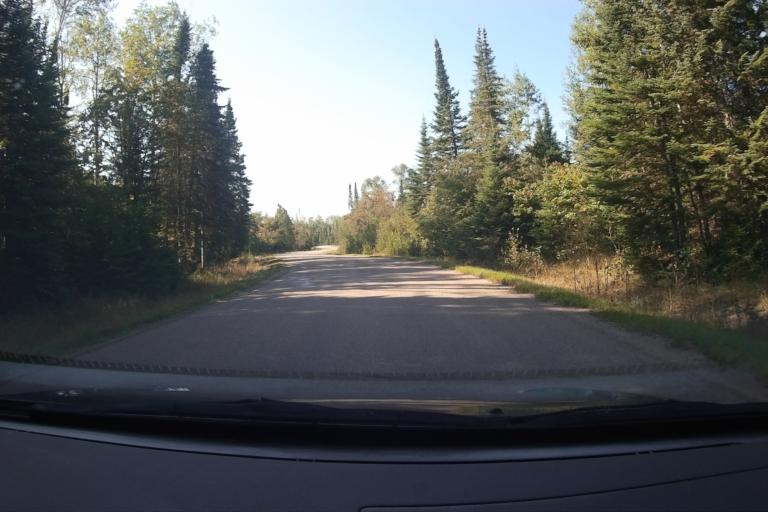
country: CA
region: Ontario
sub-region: Thunder Bay District
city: Thunder Bay
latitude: 48.3549
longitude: -88.8034
